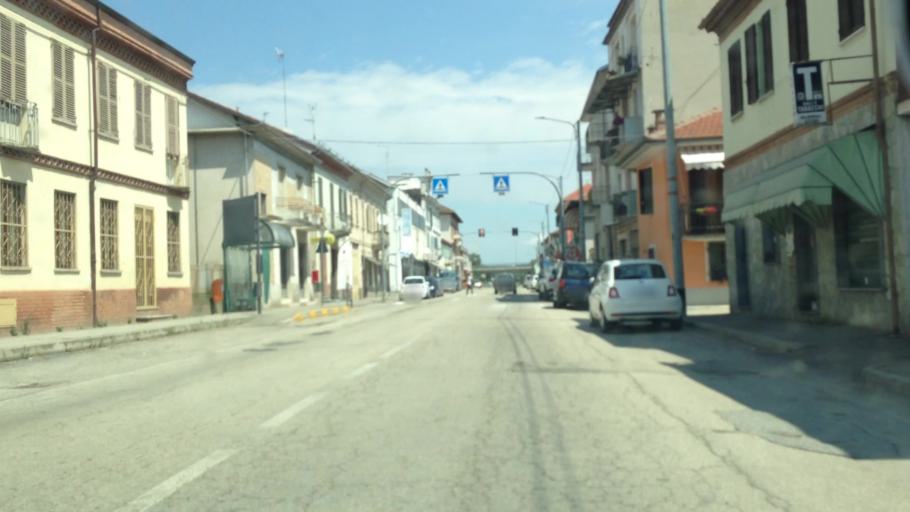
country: IT
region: Piedmont
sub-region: Provincia di Asti
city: Castell'Alfero
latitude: 44.9567
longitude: 8.2234
